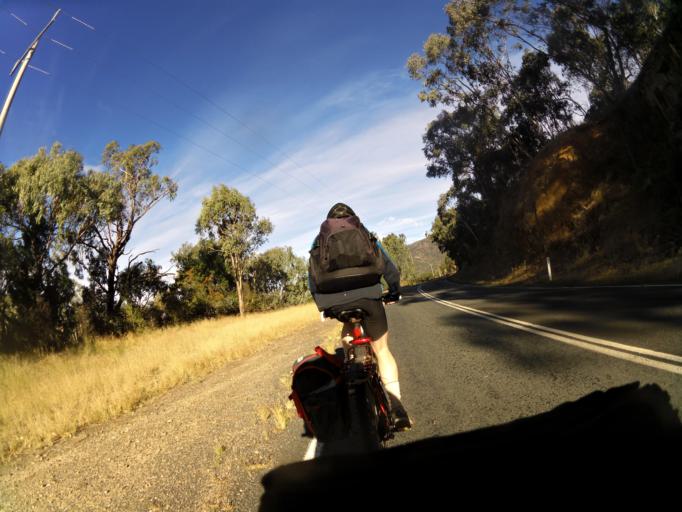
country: AU
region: New South Wales
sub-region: Greater Hume Shire
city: Holbrook
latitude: -35.9795
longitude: 147.8159
